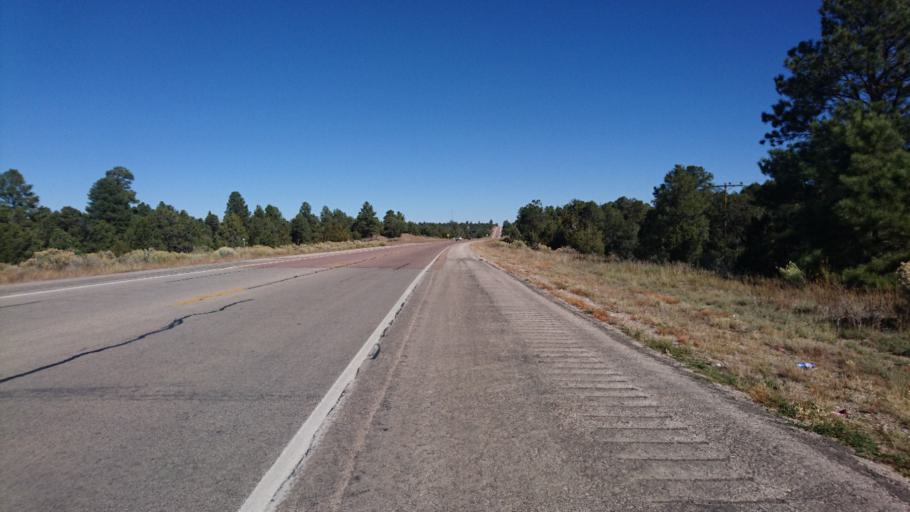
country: US
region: New Mexico
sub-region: McKinley County
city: Black Rock
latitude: 35.2308
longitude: -108.7660
